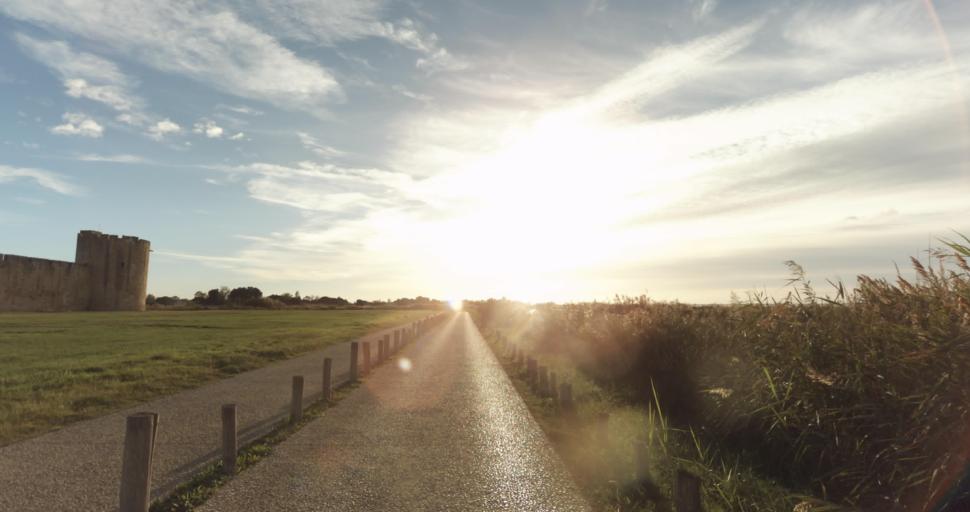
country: FR
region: Languedoc-Roussillon
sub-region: Departement du Gard
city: Aigues-Mortes
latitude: 43.5636
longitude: 4.1911
